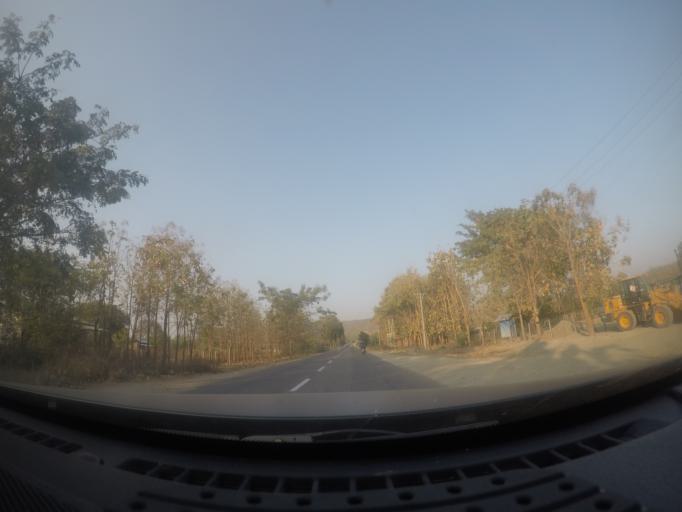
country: MM
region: Mandalay
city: Yamethin
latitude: 20.7412
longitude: 96.2128
